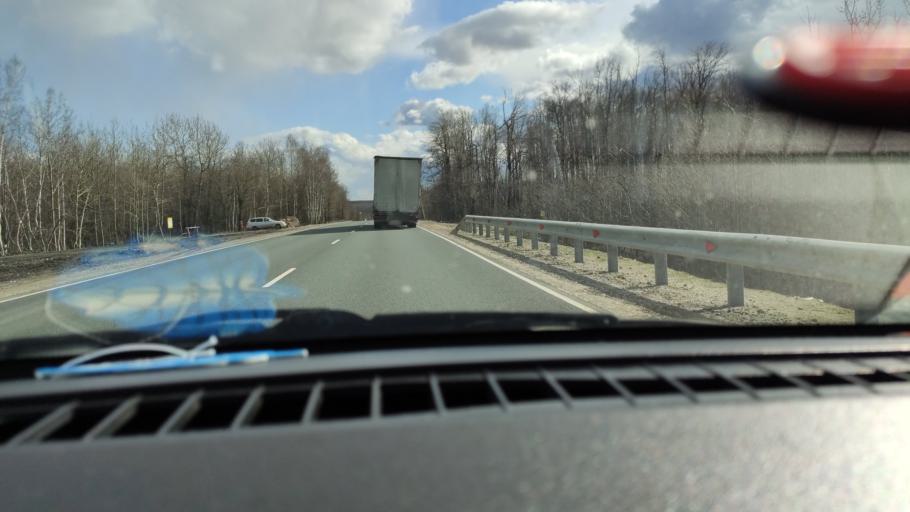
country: RU
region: Saratov
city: Alekseyevka
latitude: 52.4187
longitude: 48.0080
